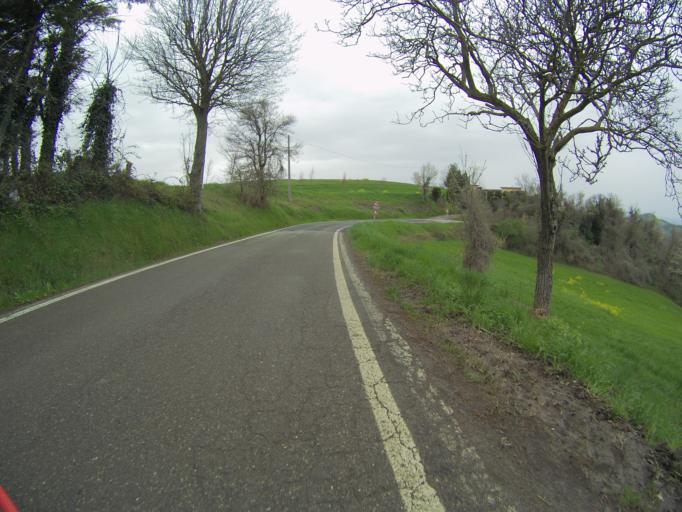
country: IT
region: Emilia-Romagna
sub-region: Provincia di Reggio Emilia
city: Ciano d'Enza
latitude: 44.5931
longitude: 10.4496
